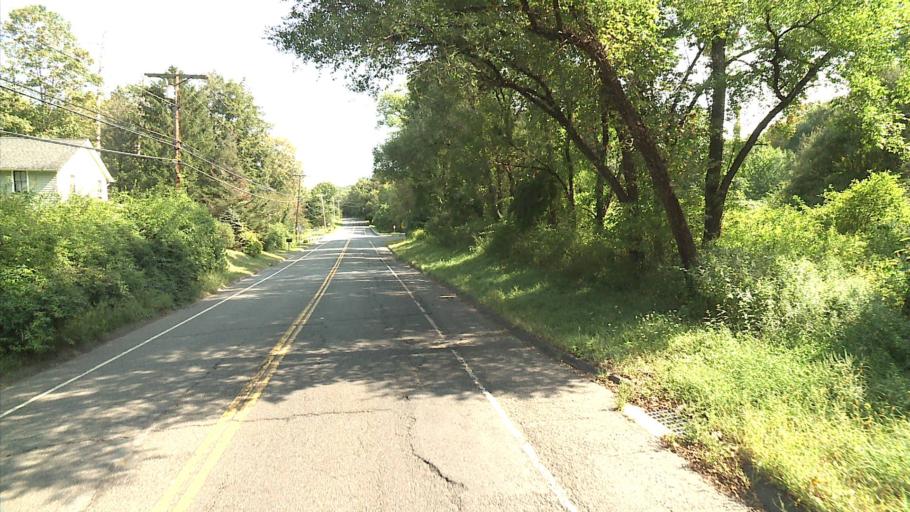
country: US
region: Connecticut
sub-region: New Haven County
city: Heritage Village
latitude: 41.4632
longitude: -73.2438
